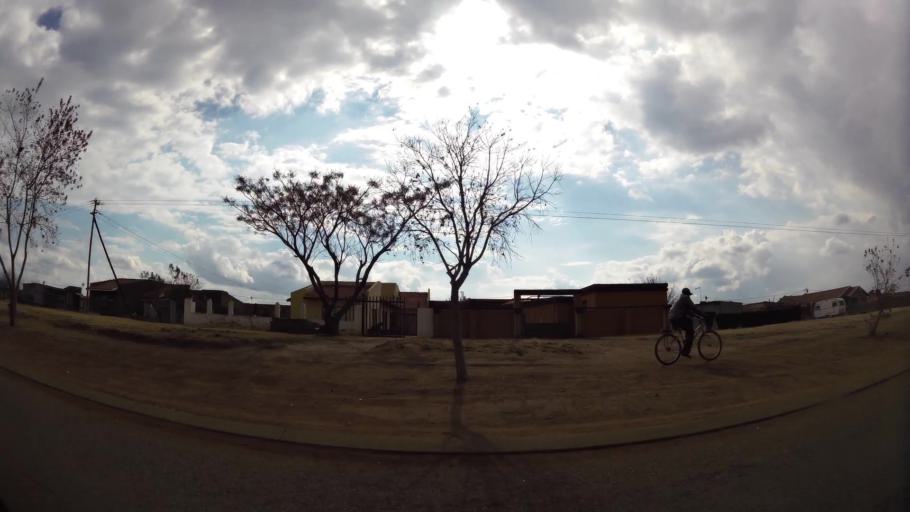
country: ZA
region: Gauteng
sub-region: Sedibeng District Municipality
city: Vanderbijlpark
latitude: -26.6808
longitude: 27.7874
